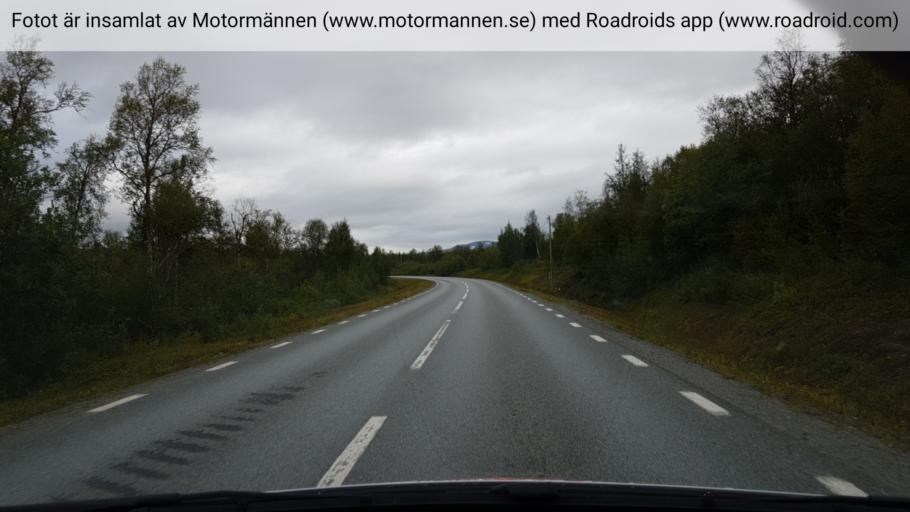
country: NO
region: Nordland
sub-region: Rana
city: Mo i Rana
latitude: 66.0167
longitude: 15.0904
